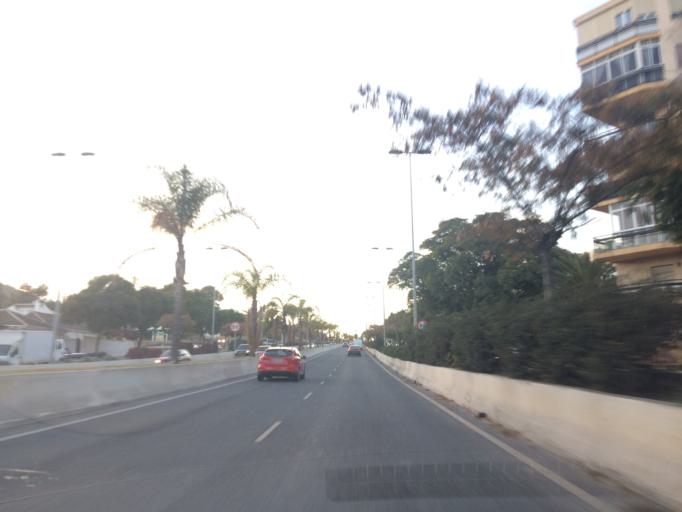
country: ES
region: Andalusia
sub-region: Provincia de Malaga
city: Torremolinos
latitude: 36.6608
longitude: -4.5002
